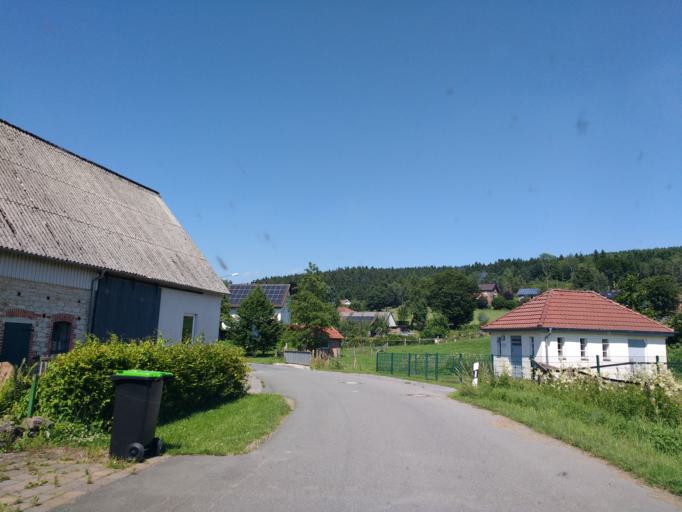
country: DE
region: North Rhine-Westphalia
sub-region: Regierungsbezirk Detmold
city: Horn
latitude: 51.8267
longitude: 8.9403
